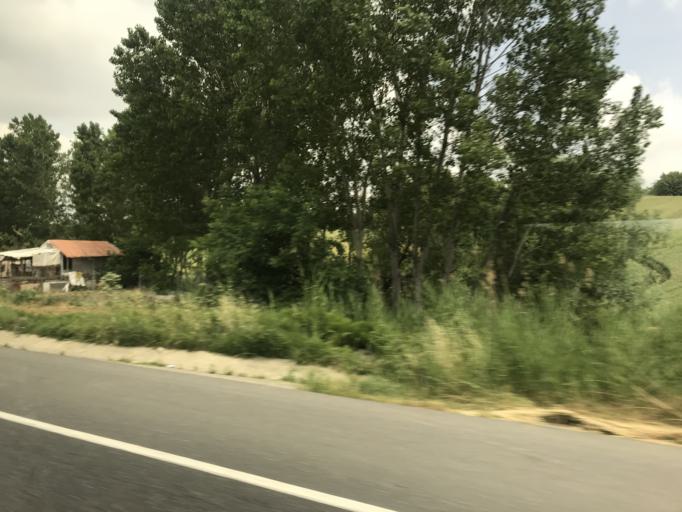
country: TR
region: Tekirdag
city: Tekirdag
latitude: 40.9975
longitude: 27.5538
